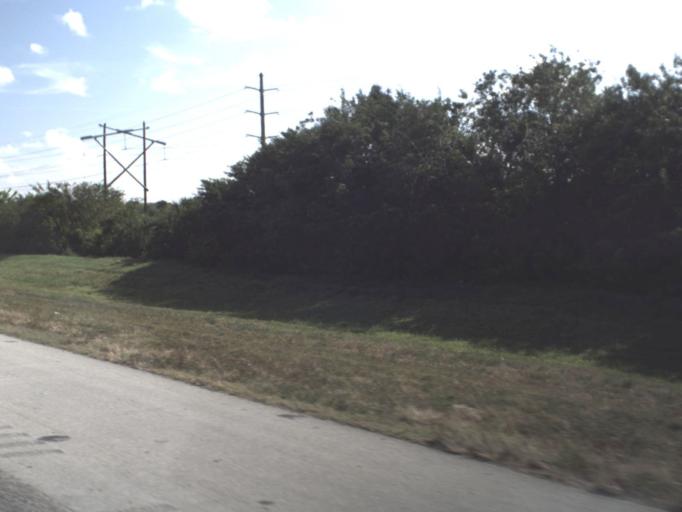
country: US
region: Florida
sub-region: Brevard County
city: June Park
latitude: 28.1336
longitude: -80.7061
